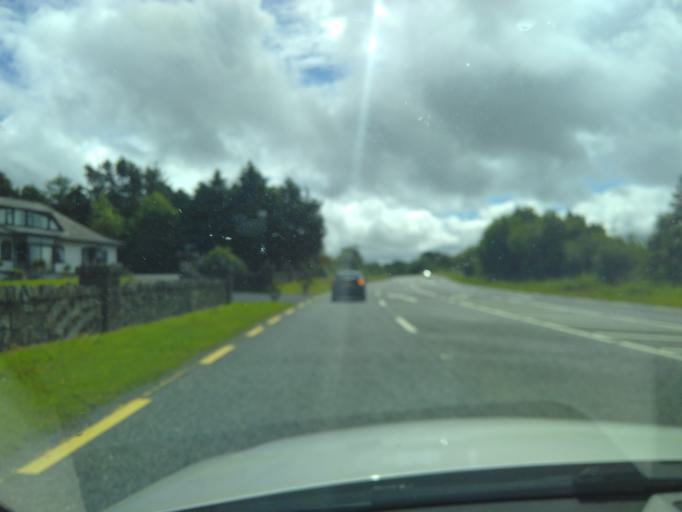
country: IE
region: Ulster
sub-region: County Donegal
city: Letterkenny
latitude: 54.9294
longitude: -7.6954
